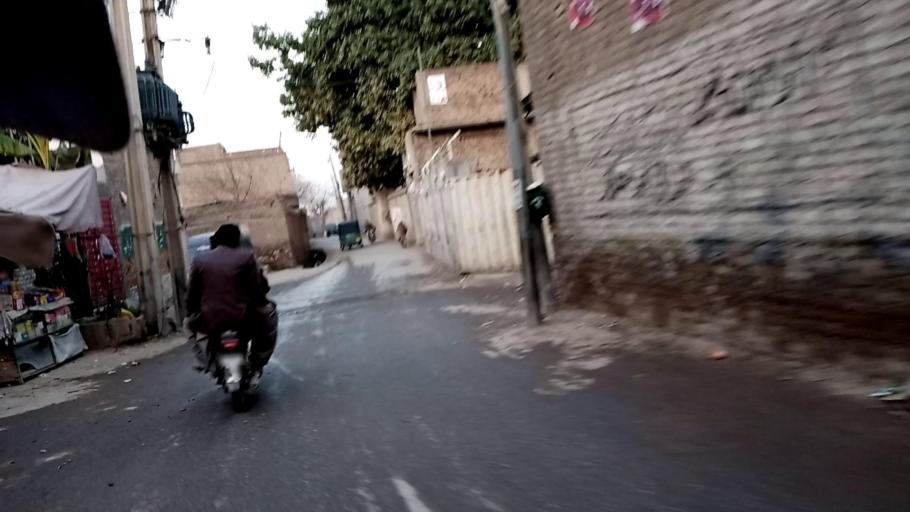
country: PK
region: Khyber Pakhtunkhwa
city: Peshawar
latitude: 34.0301
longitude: 71.4901
